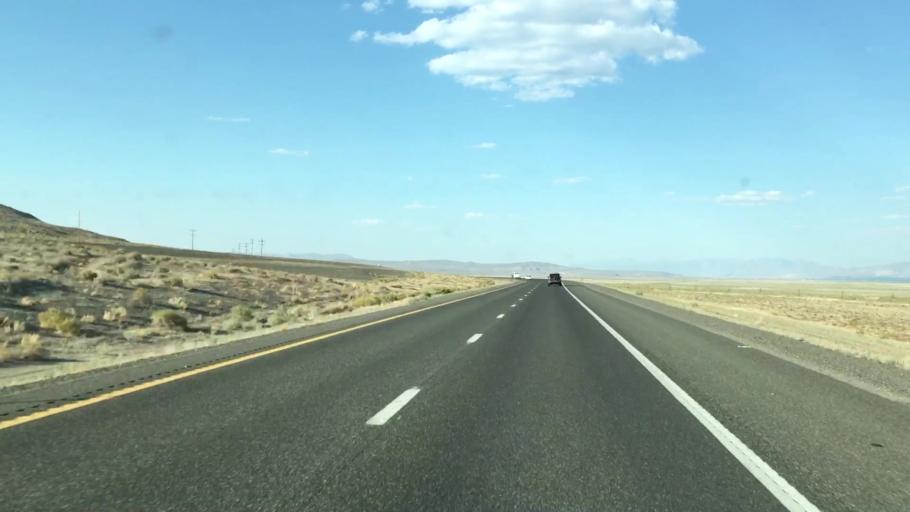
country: US
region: Nevada
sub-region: Pershing County
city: Lovelock
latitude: 39.9850
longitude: -118.6867
